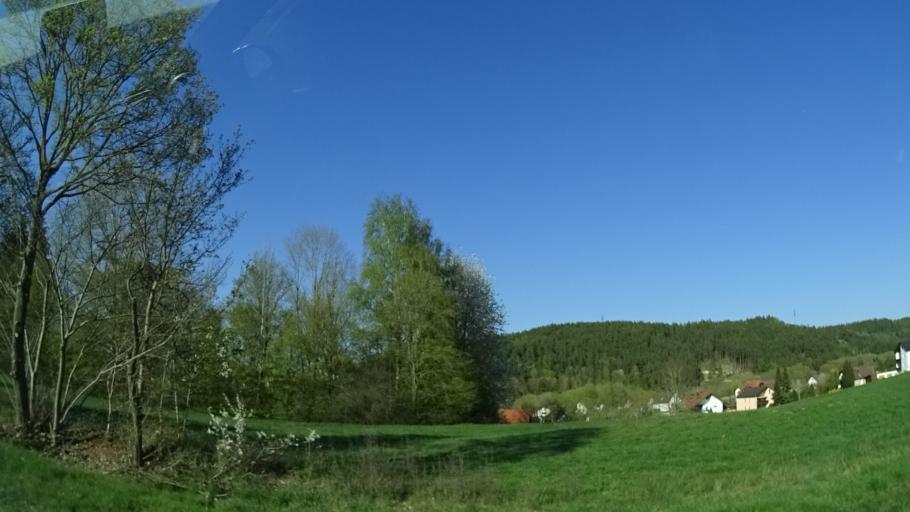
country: DE
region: Bavaria
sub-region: Upper Palatinate
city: Auerbach
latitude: 49.6835
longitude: 11.6357
